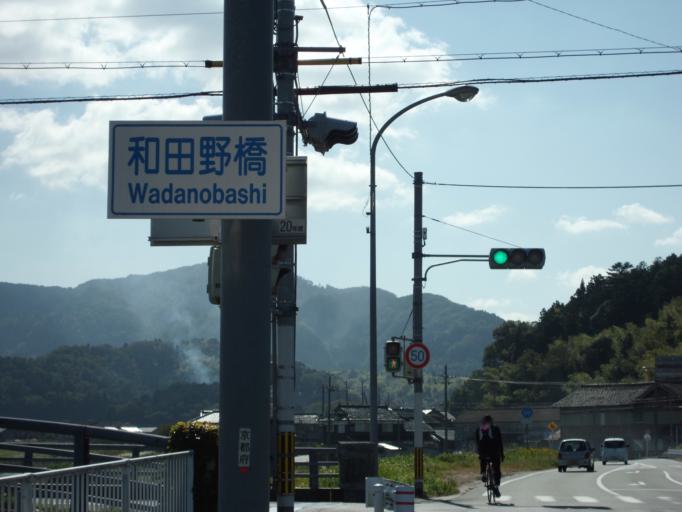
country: JP
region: Kyoto
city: Miyazu
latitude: 35.6602
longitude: 135.0869
